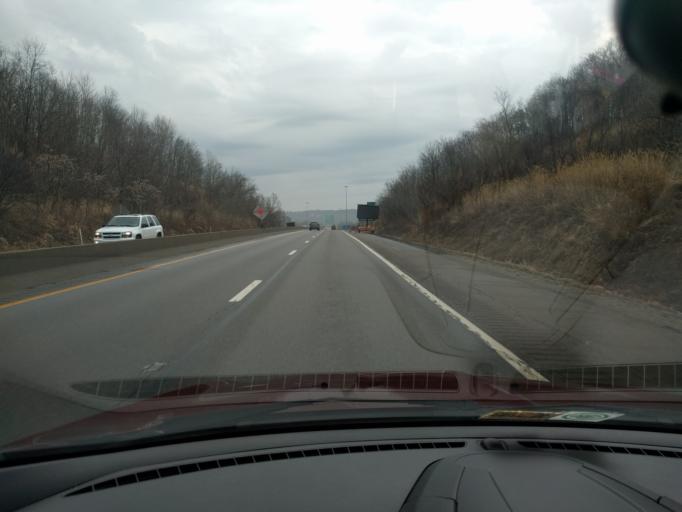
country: US
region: West Virginia
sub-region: Wood County
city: Williamstown
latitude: 39.3958
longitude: -81.4376
